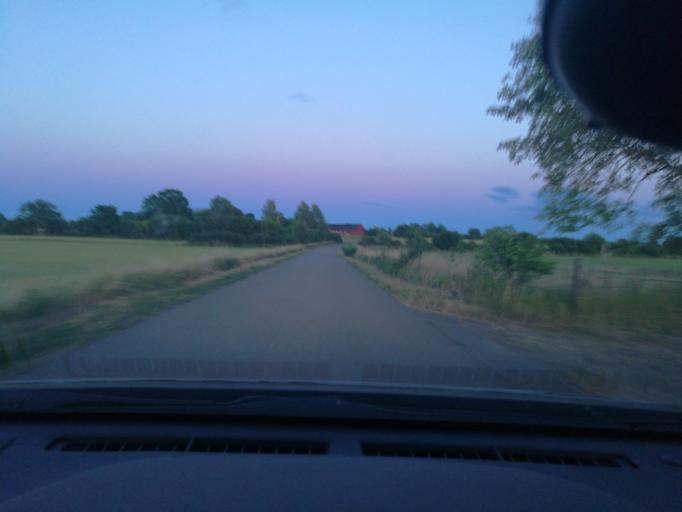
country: SE
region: Kalmar
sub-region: Borgholms Kommun
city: Borgholm
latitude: 56.8651
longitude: 16.7501
